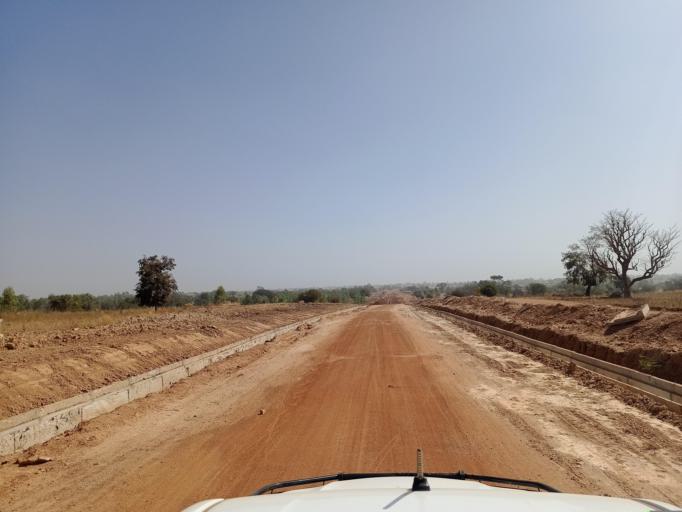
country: BF
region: Centre-Est
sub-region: Province du Boulgou
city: Garango
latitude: 11.5014
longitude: -0.5063
